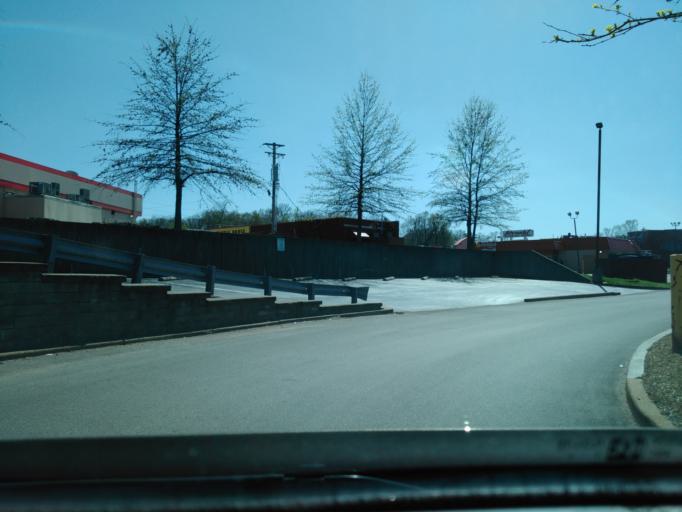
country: US
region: Missouri
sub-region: Saint Louis County
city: Concord
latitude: 38.4866
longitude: -90.3573
